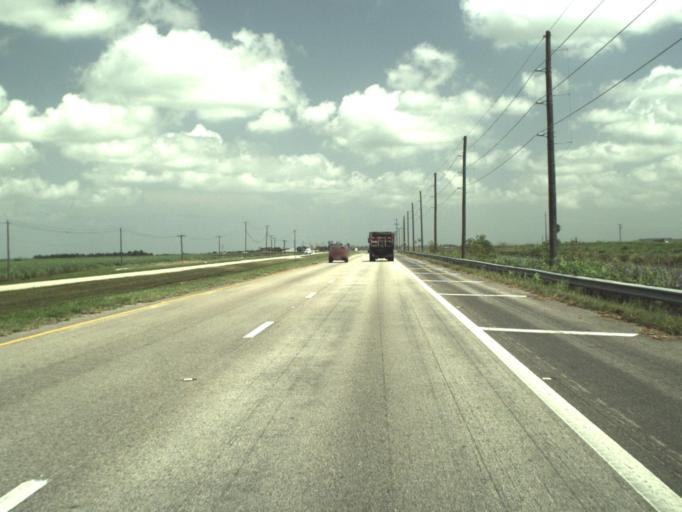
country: US
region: Florida
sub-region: Palm Beach County
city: South Bay
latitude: 26.6050
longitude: -80.7114
